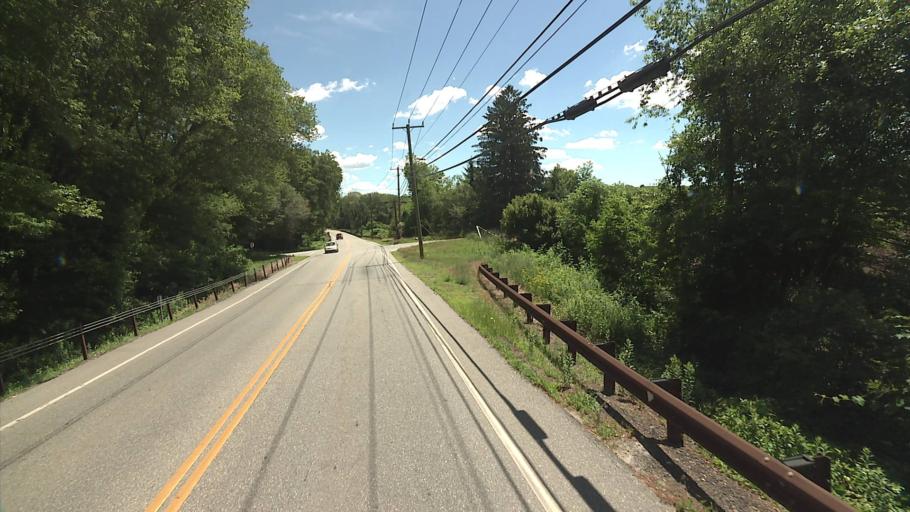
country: US
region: Rhode Island
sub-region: Washington County
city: Ashaway
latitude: 41.4367
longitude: -71.8127
